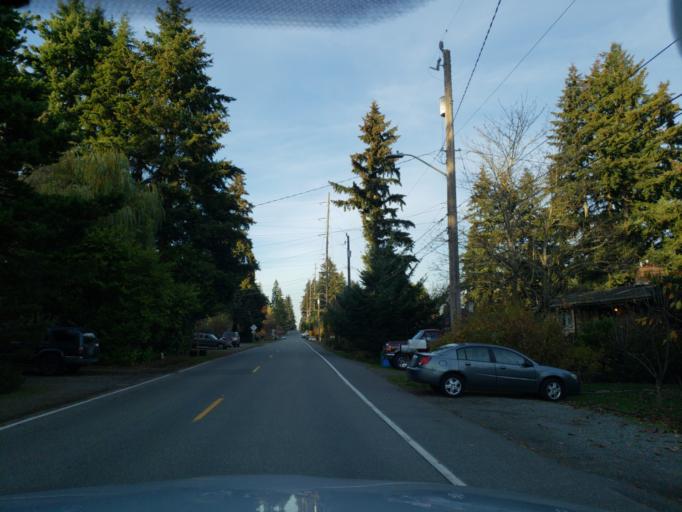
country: US
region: Washington
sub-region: King County
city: Shoreline
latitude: 47.7441
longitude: -122.3400
